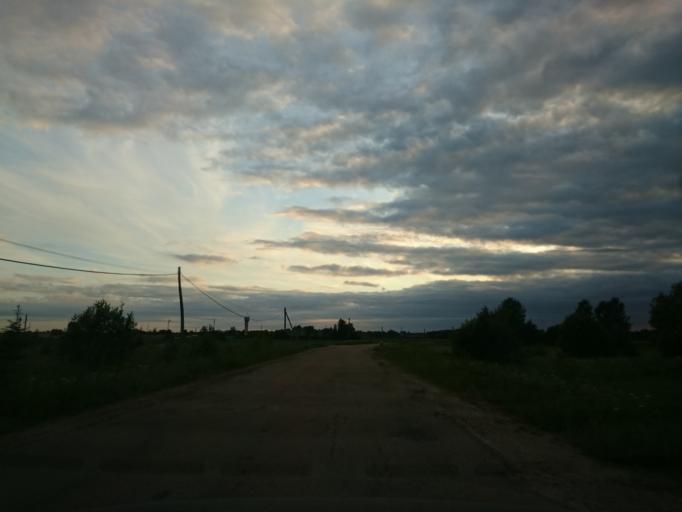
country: LV
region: Ropazu
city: Ropazi
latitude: 56.9578
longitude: 24.6992
